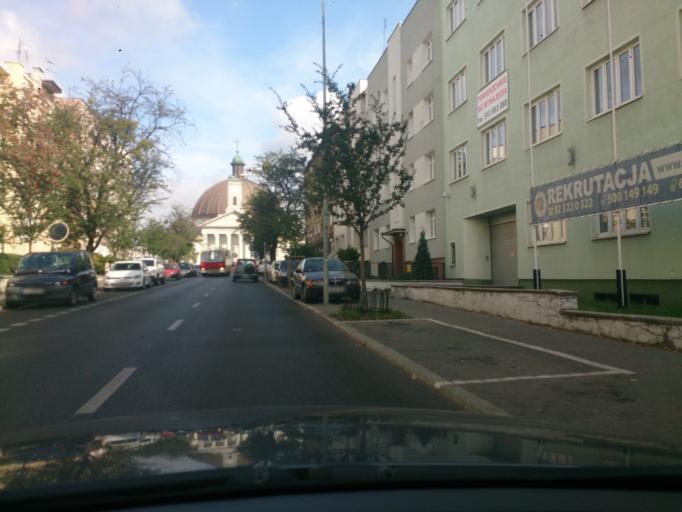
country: PL
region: Kujawsko-Pomorskie
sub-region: Bydgoszcz
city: Bydgoszcz
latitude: 53.1247
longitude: 18.0160
